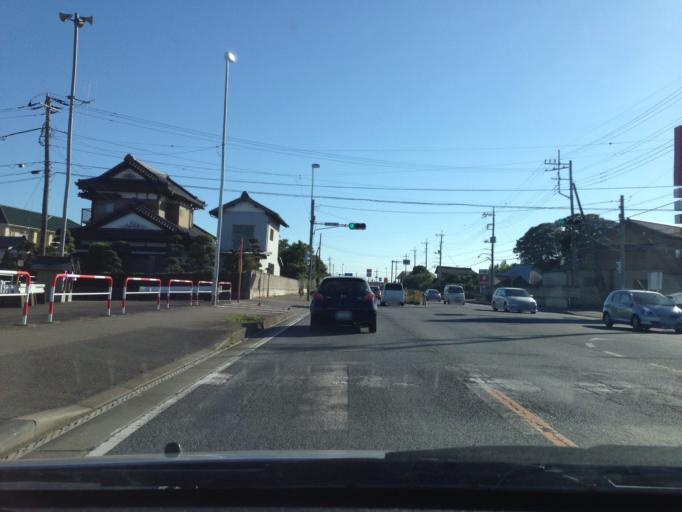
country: JP
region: Ibaraki
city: Naka
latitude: 36.0411
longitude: 140.1787
